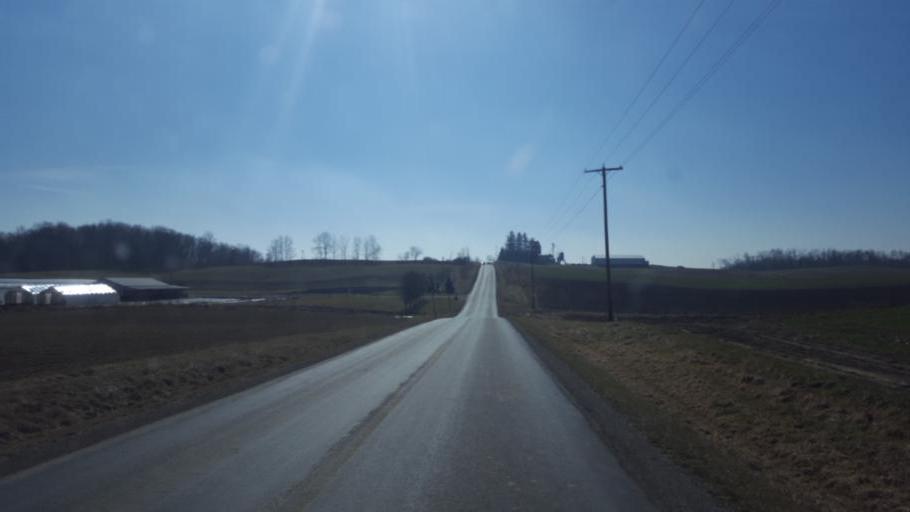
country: US
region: Ohio
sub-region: Huron County
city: Plymouth
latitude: 40.9548
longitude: -82.5847
